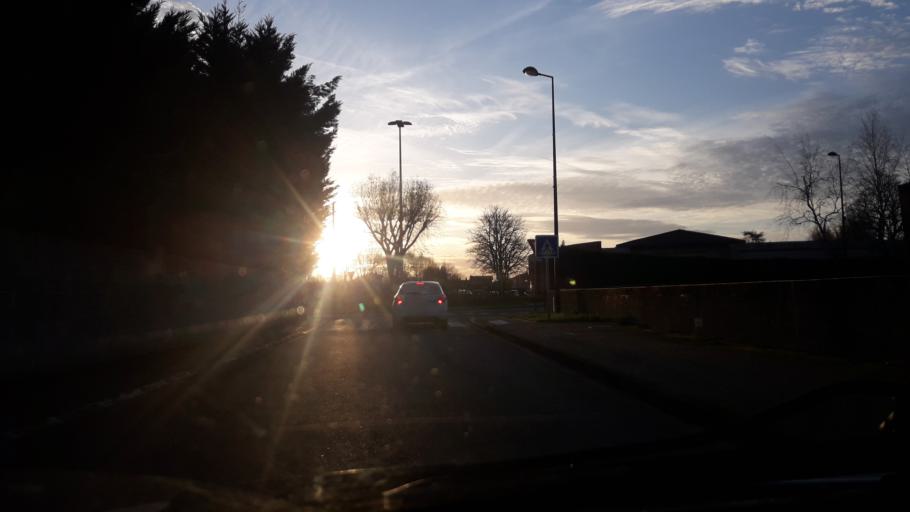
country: FR
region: Midi-Pyrenees
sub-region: Departement de la Haute-Garonne
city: Labastidette
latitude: 43.4843
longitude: 1.2425
